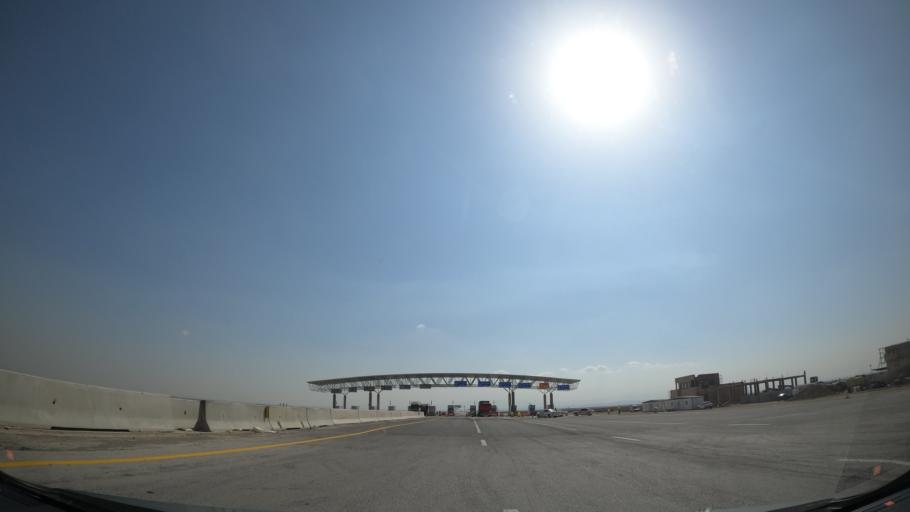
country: IR
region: Qazvin
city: Abyek
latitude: 35.9593
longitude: 50.4643
